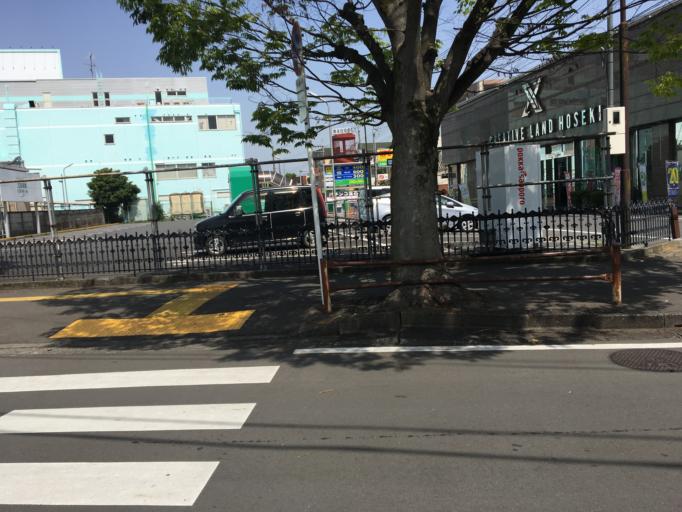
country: JP
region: Saitama
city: Iwatsuki
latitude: 35.9640
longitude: 139.7121
